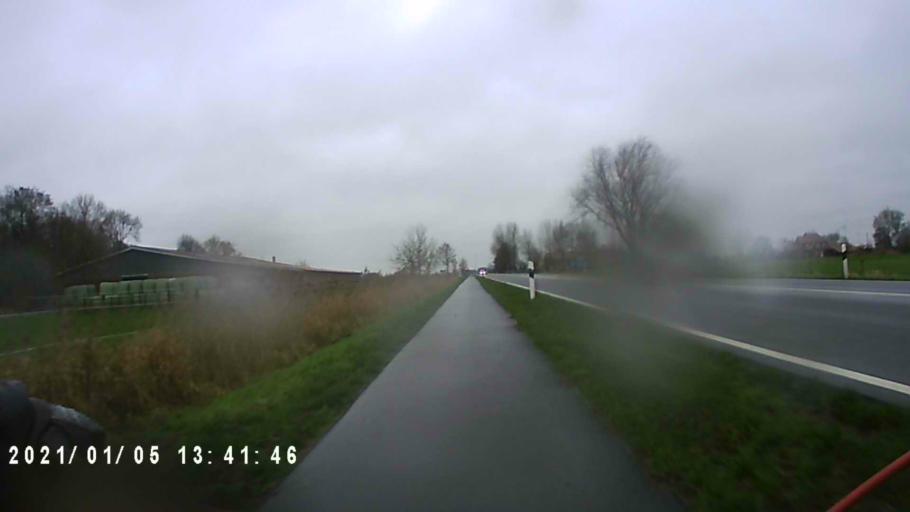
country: DE
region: Lower Saxony
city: Weener
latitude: 53.2015
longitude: 7.4004
